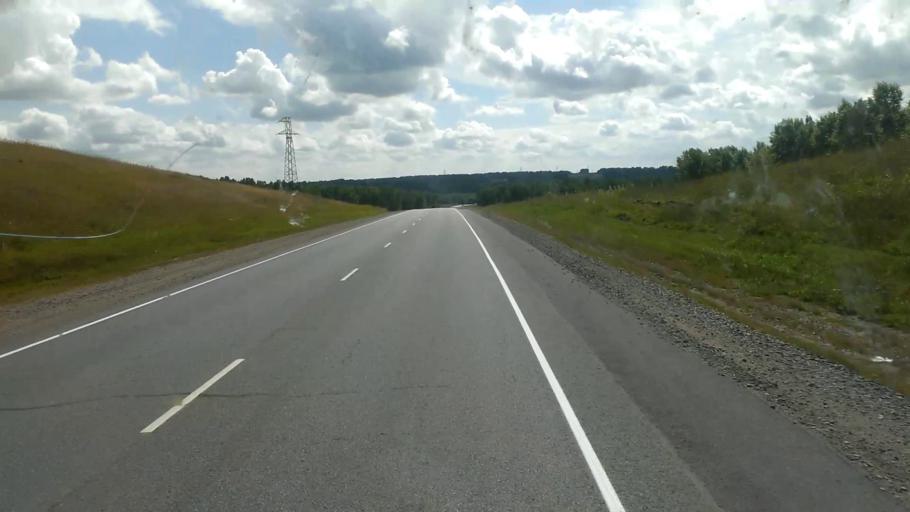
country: RU
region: Altai Krai
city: Troitskoye
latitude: 52.9443
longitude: 84.7755
